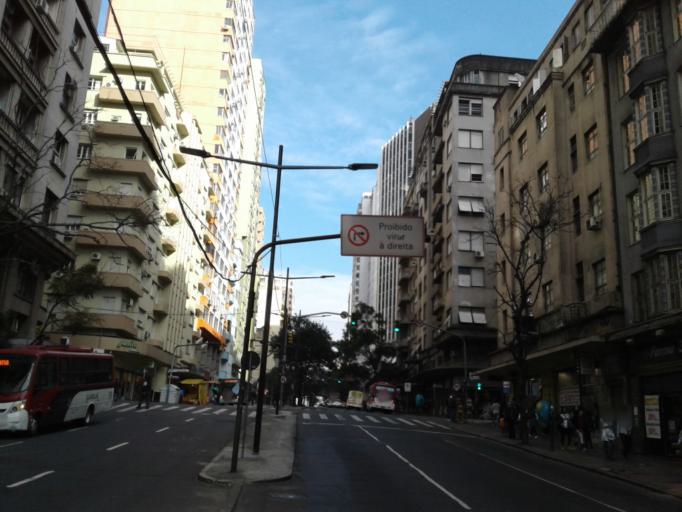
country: BR
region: Rio Grande do Sul
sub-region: Porto Alegre
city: Porto Alegre
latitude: -30.0312
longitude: -51.2279
